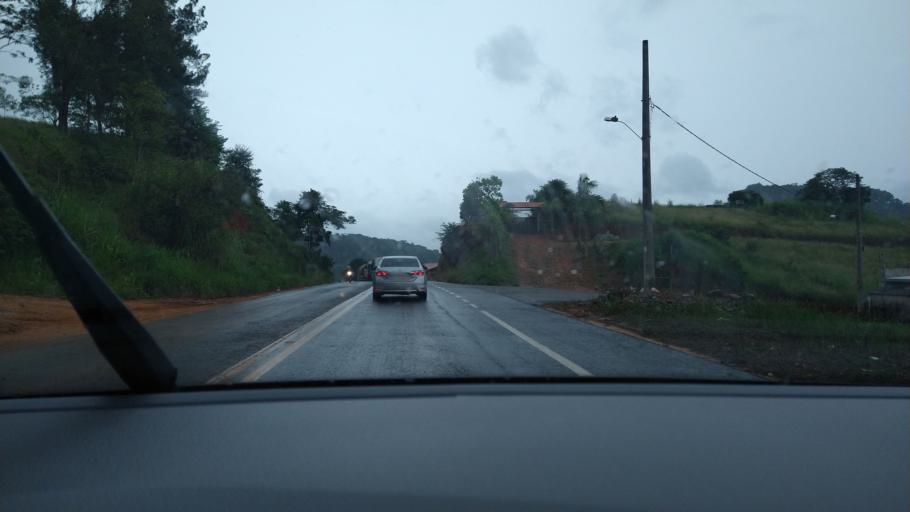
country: BR
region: Minas Gerais
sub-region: Vicosa
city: Vicosa
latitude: -20.6468
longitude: -42.8657
